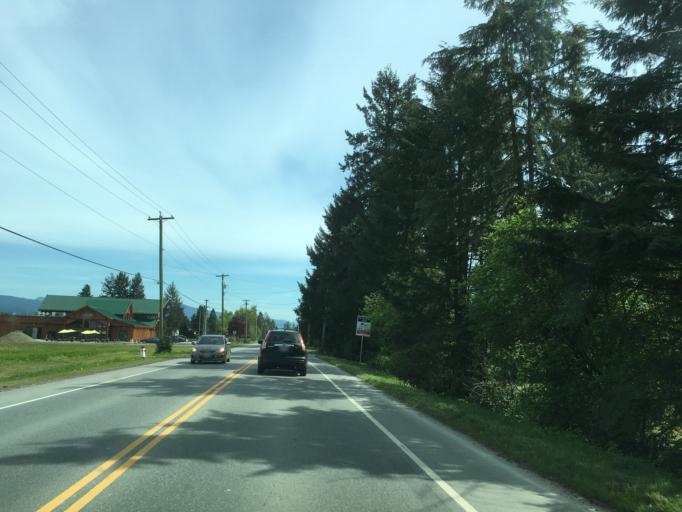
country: CA
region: British Columbia
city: Pitt Meadows
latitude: 49.2443
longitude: -122.7147
